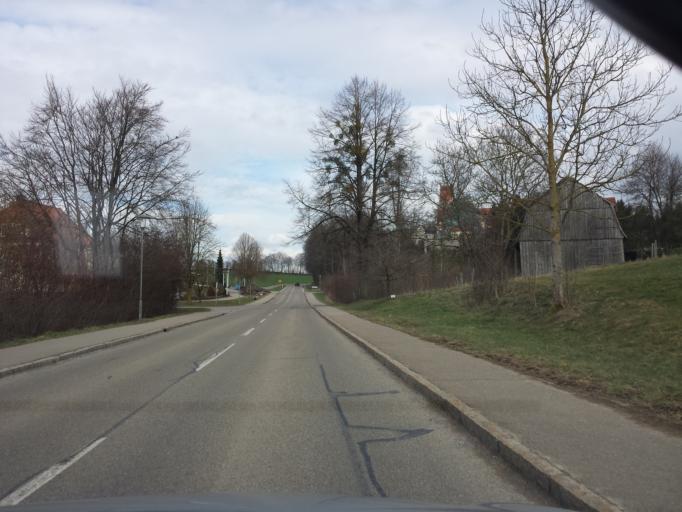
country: DE
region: Baden-Wuerttemberg
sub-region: Tuebingen Region
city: Huttisheim
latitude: 48.2775
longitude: 9.9465
